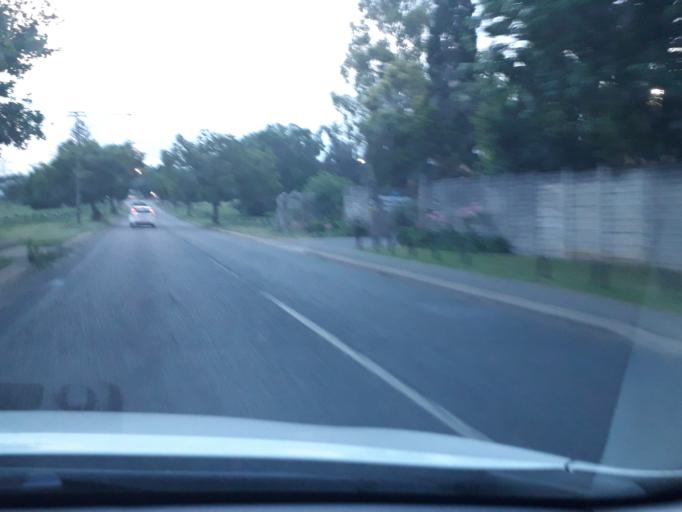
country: ZA
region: Gauteng
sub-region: City of Johannesburg Metropolitan Municipality
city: Johannesburg
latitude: -26.1448
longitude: 28.0023
